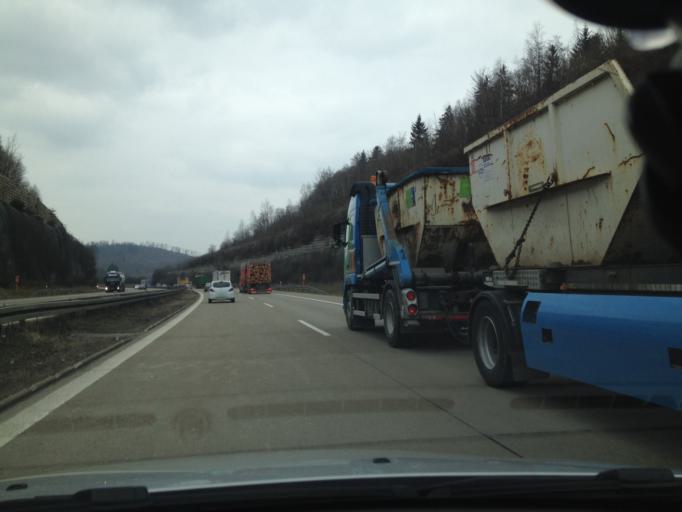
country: DE
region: Baden-Wuerttemberg
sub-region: Regierungsbezirk Stuttgart
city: Westhausen
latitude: 48.8612
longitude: 10.1943
